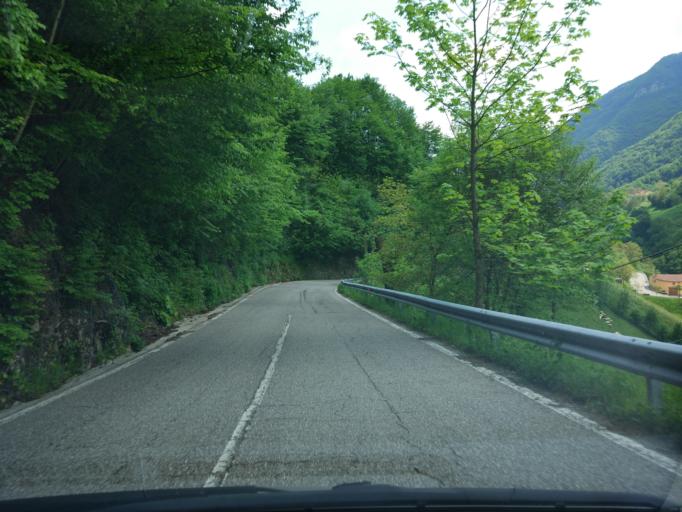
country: IT
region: Veneto
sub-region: Provincia di Verona
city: Selva di Progno
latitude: 45.6349
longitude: 11.1292
